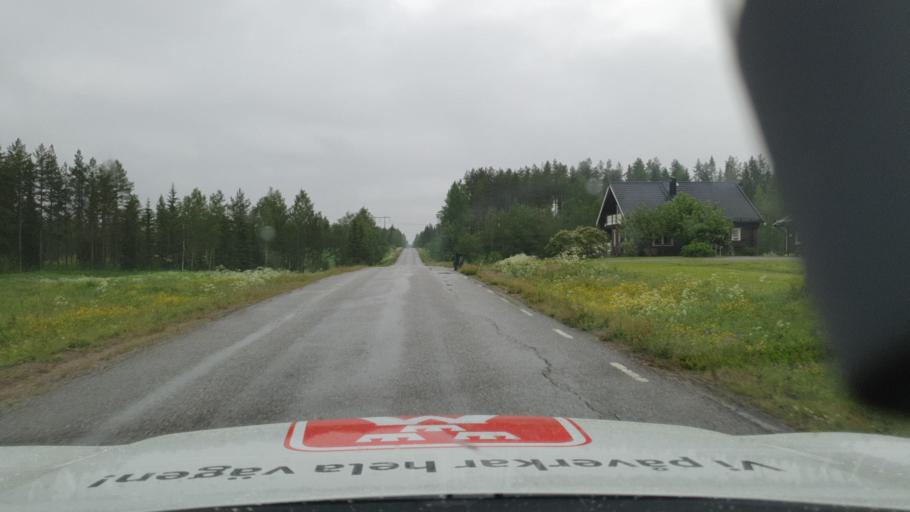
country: SE
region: Vaesterbotten
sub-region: Nordmalings Kommun
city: Nordmaling
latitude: 63.8112
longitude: 19.5000
